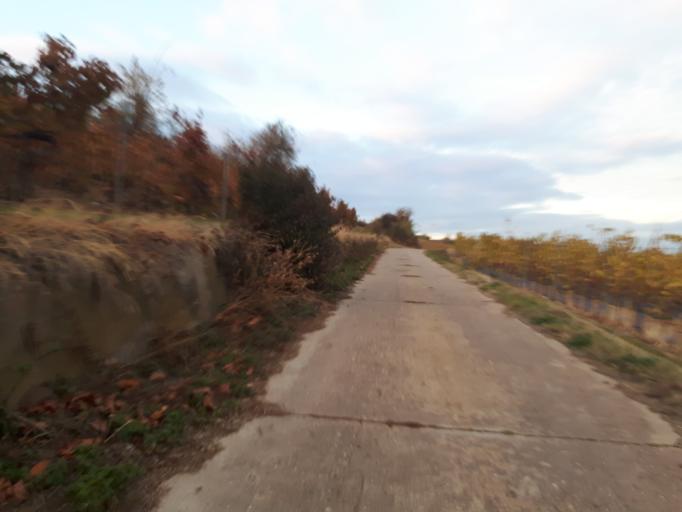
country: DE
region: Rheinland-Pfalz
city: Molsheim
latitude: 49.6529
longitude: 8.1886
